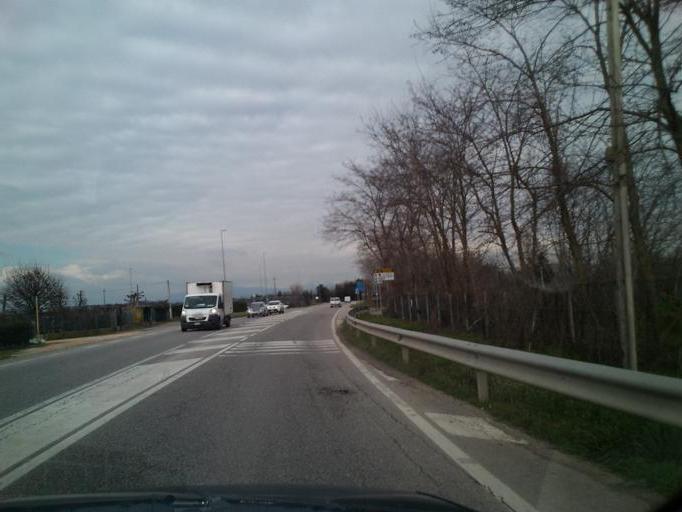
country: IT
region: Veneto
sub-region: Provincia di Verona
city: Villafranca di Verona
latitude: 45.3804
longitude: 10.8465
